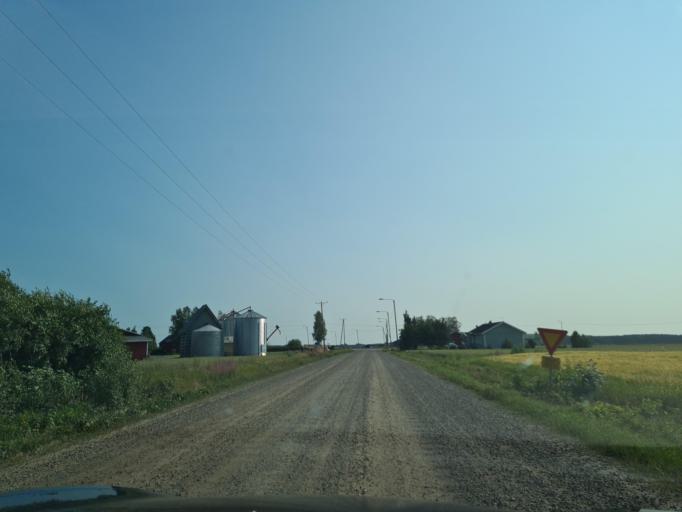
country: FI
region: Ostrobothnia
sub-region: Kyroenmaa
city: Laihia
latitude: 63.0029
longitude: 21.9034
